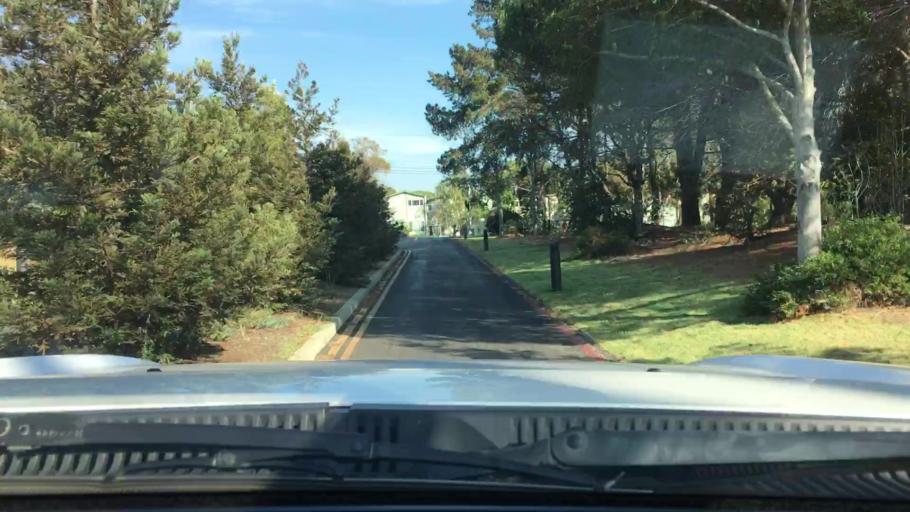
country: US
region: California
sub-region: San Luis Obispo County
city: San Luis Obispo
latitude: 35.2637
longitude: -120.6432
